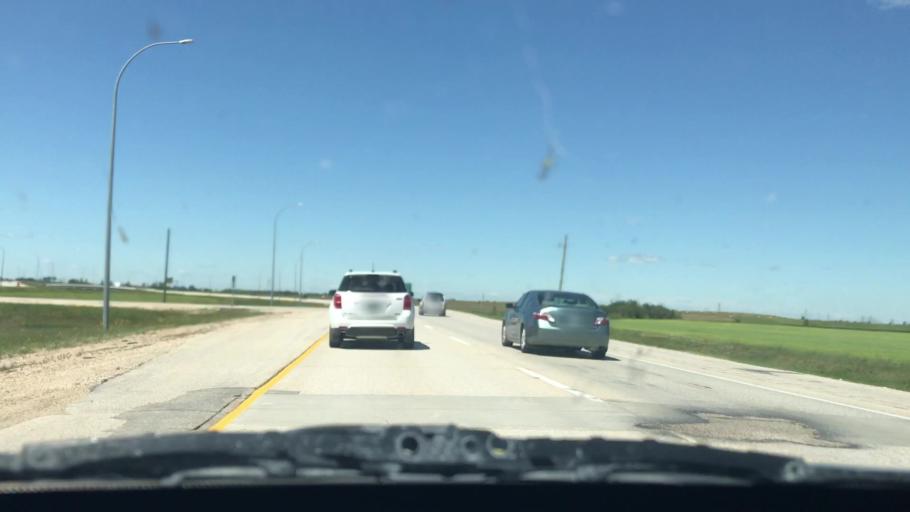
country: CA
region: Manitoba
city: Winnipeg
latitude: 49.8260
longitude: -96.9463
